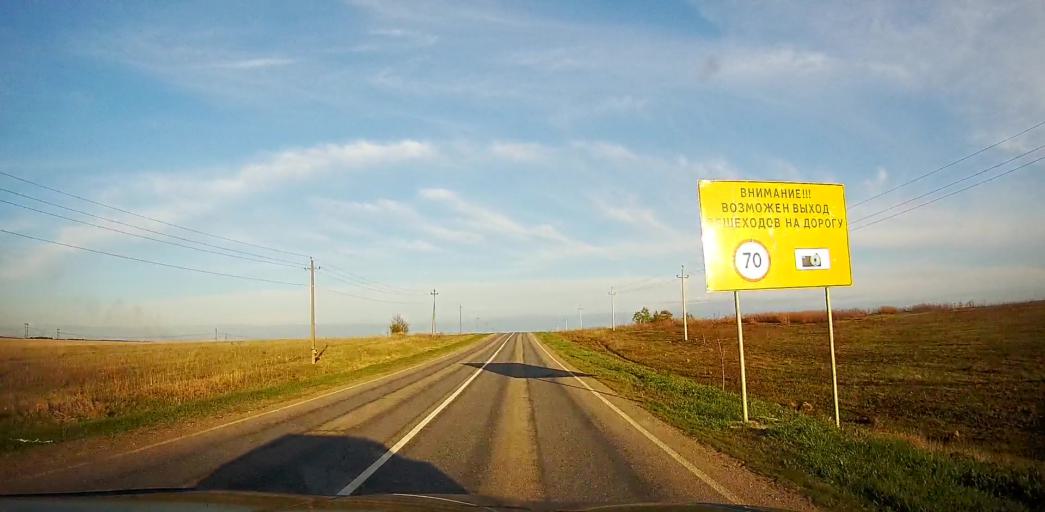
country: RU
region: Moskovskaya
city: Meshcherino
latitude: 55.2690
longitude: 38.2446
